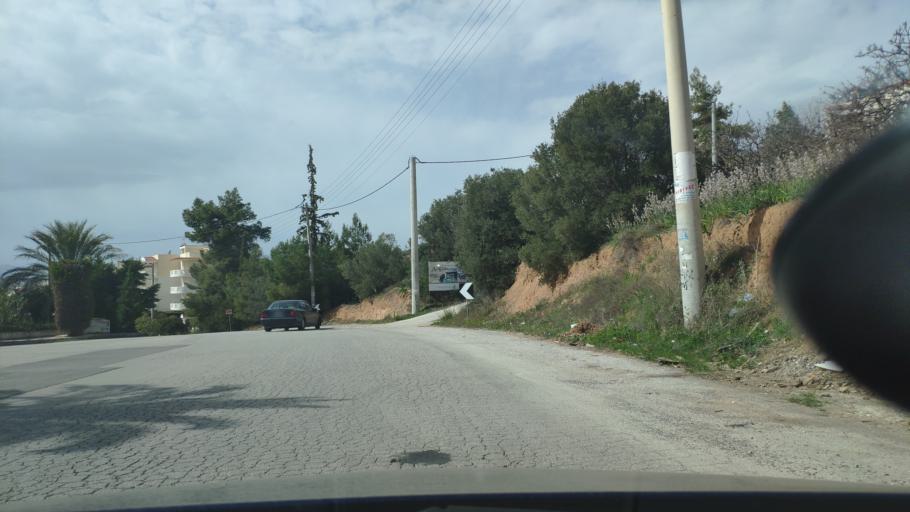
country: GR
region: Attica
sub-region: Nomarchia Anatolikis Attikis
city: Limin Mesoyaias
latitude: 37.8953
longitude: 24.0150
